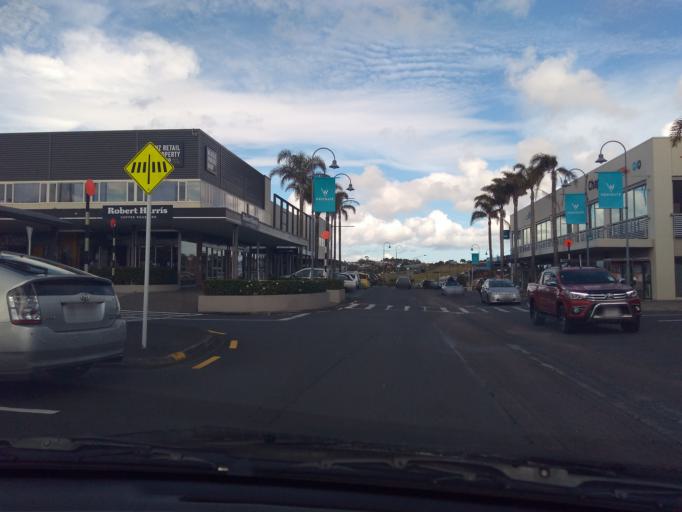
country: NZ
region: Auckland
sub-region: Auckland
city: Rosebank
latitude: -36.8212
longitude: 174.6134
